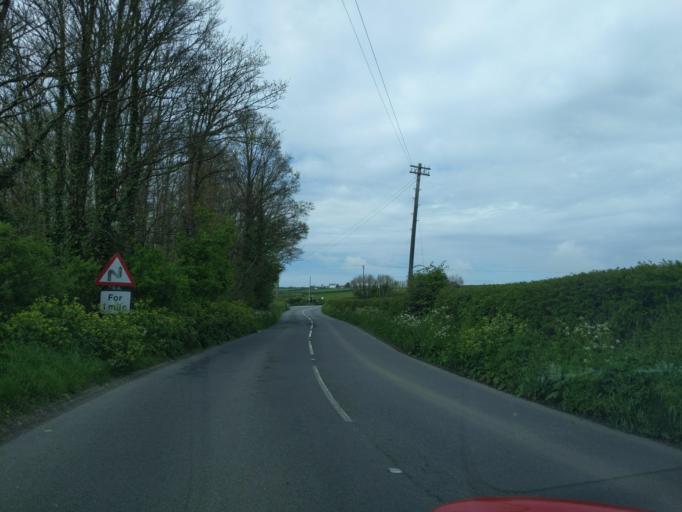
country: GB
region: England
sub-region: Cornwall
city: Wadebridge
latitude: 50.5423
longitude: -4.8618
